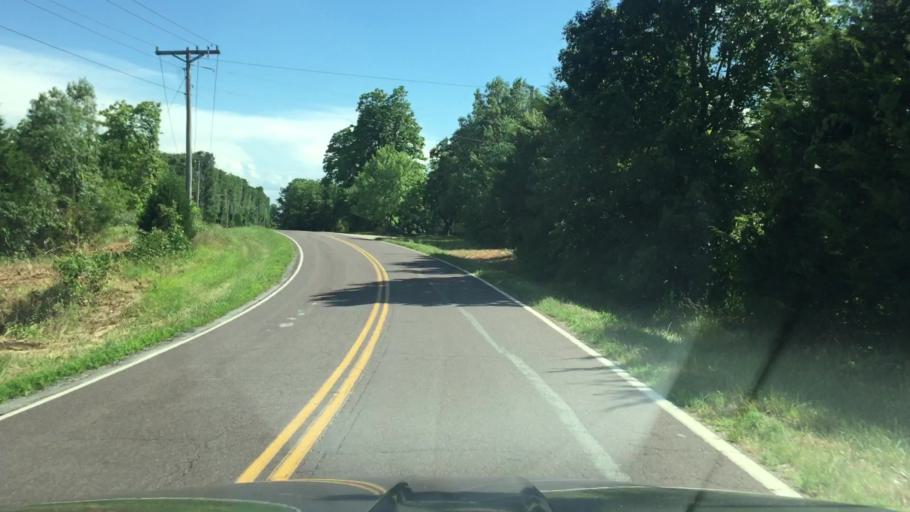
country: US
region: Missouri
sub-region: Miller County
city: Tuscumbia
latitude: 38.1176
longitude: -92.4716
